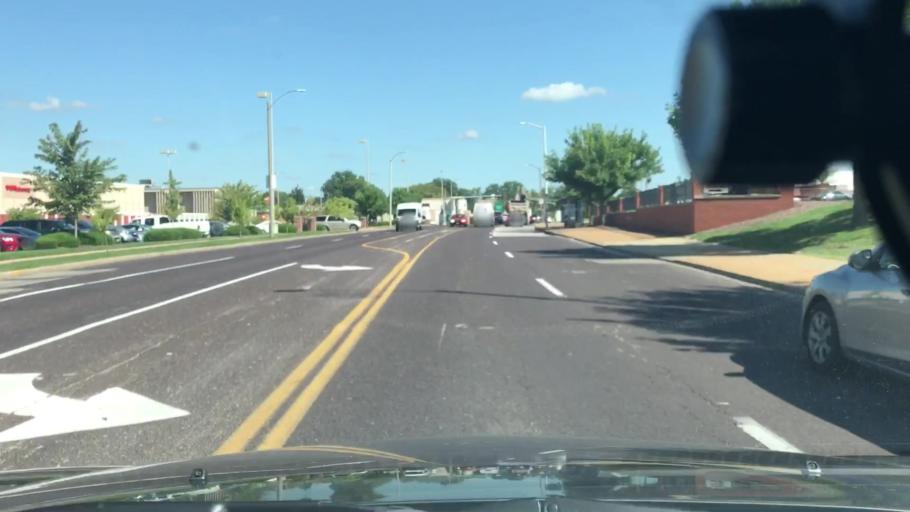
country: US
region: Missouri
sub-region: Saint Louis County
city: Maplewood
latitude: 38.5918
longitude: -90.2945
